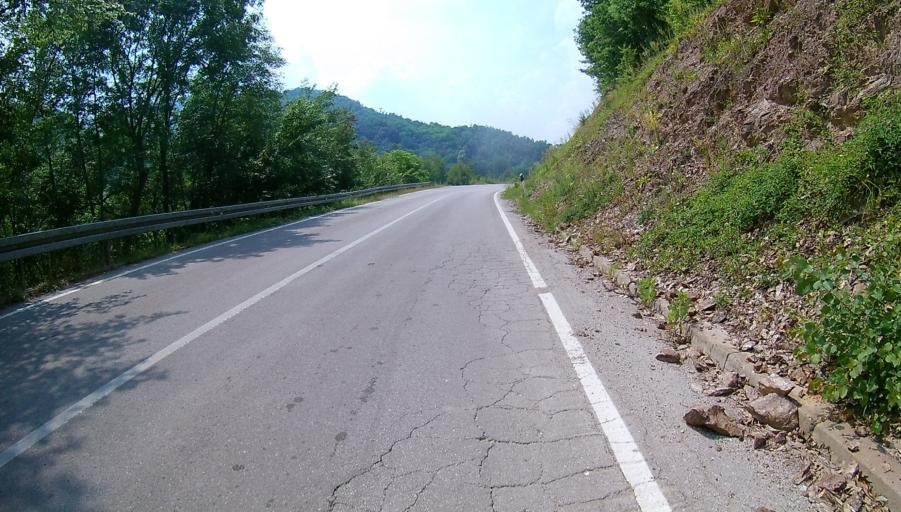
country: RS
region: Central Serbia
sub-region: Nisavski Okrug
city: Gadzin Han
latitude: 43.1679
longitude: 22.0789
